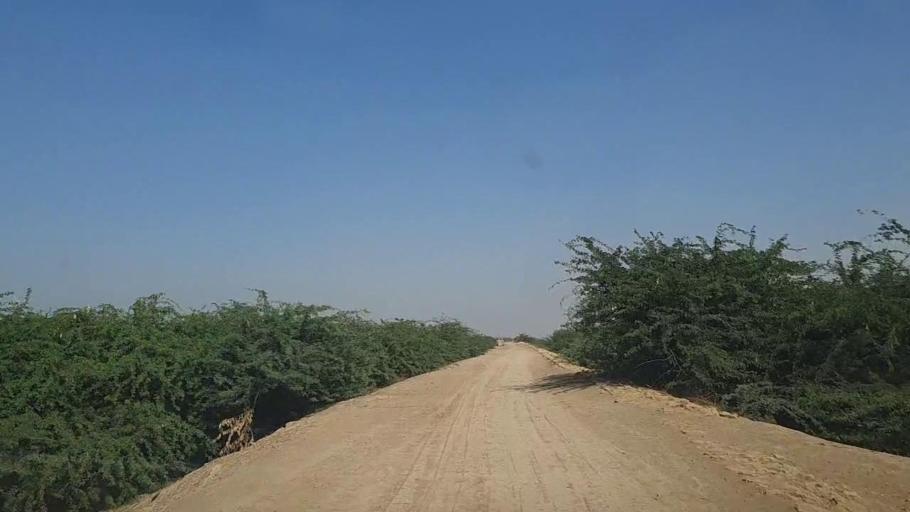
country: PK
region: Sindh
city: Daro Mehar
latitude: 24.8724
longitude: 68.0489
